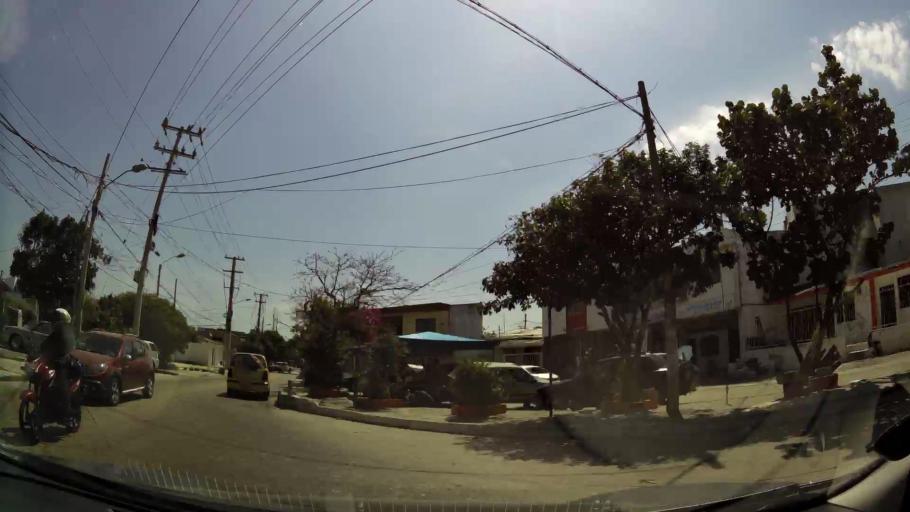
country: CO
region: Atlantico
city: Barranquilla
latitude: 10.9808
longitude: -74.8186
